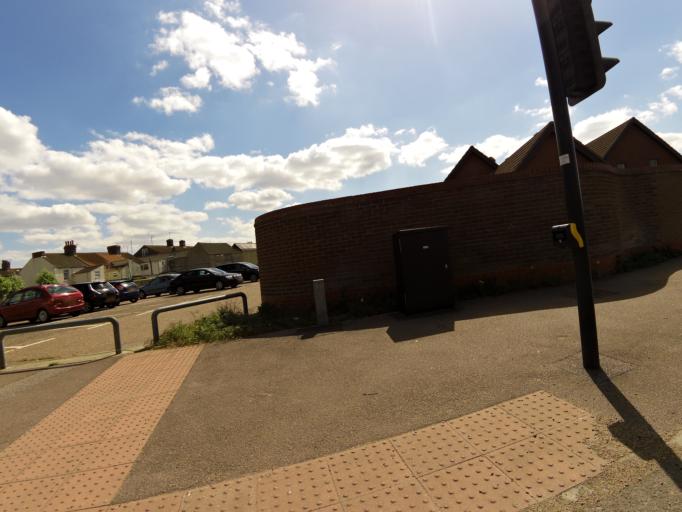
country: GB
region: England
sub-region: Suffolk
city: Lowestoft
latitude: 52.4720
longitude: 1.7465
